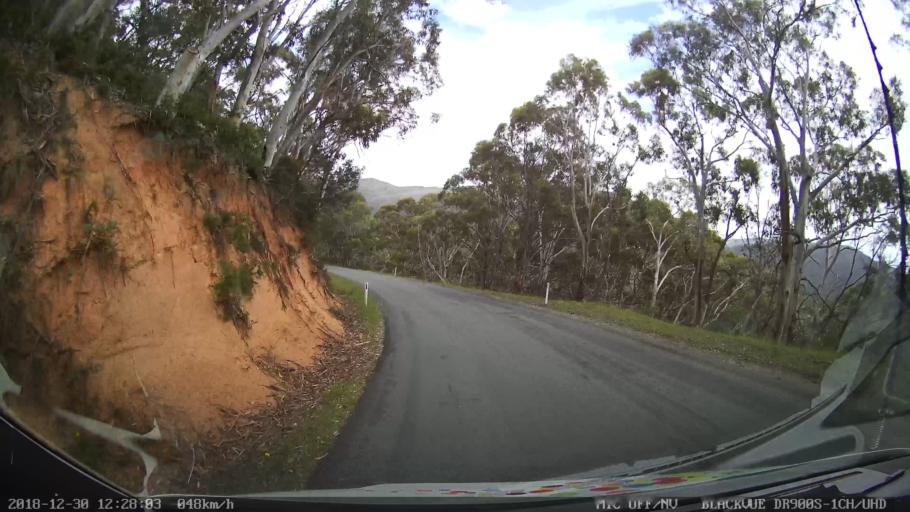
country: AU
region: New South Wales
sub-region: Snowy River
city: Jindabyne
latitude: -36.3268
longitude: 148.4882
